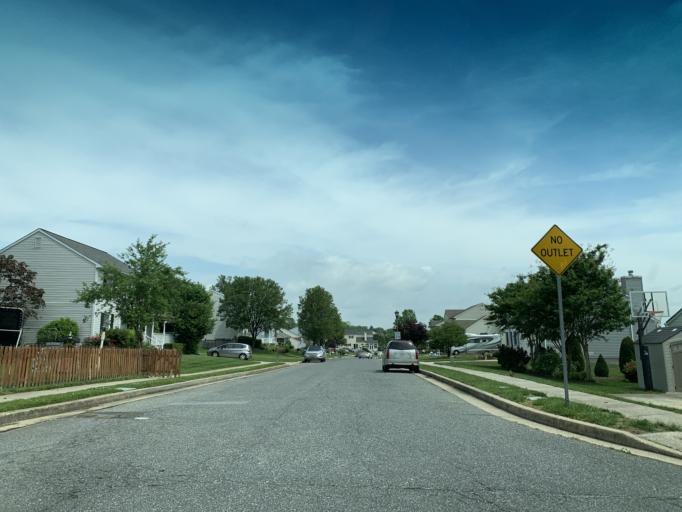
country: US
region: Maryland
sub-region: Baltimore County
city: Perry Hall
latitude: 39.4048
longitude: -76.4676
